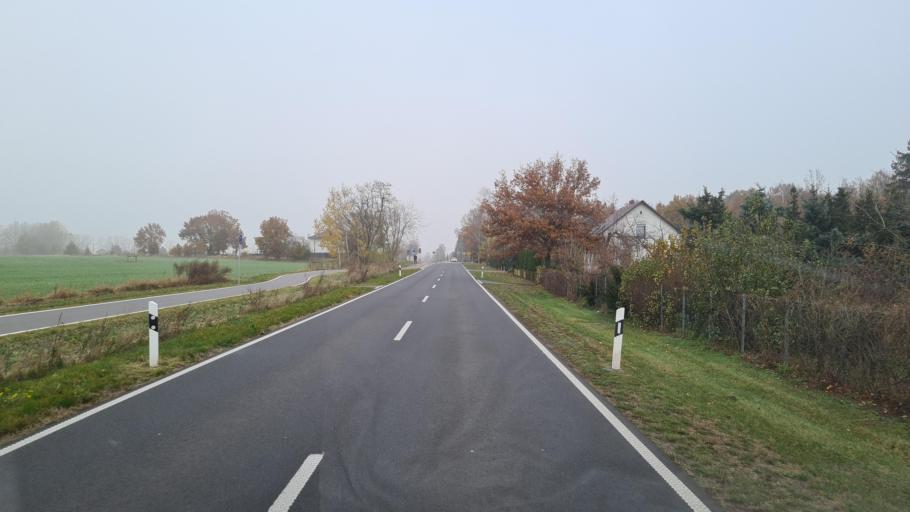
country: DE
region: Brandenburg
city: Gross Kreutz
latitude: 52.3694
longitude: 12.7644
